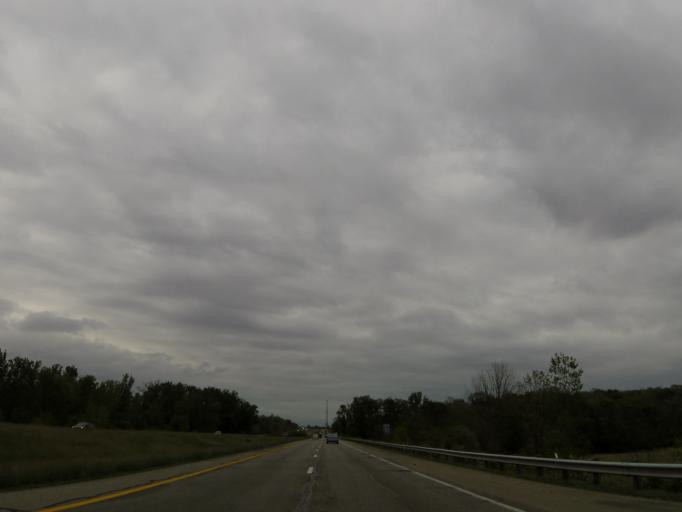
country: US
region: Ohio
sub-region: Madison County
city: Mount Sterling
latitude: 39.7617
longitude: -83.2942
